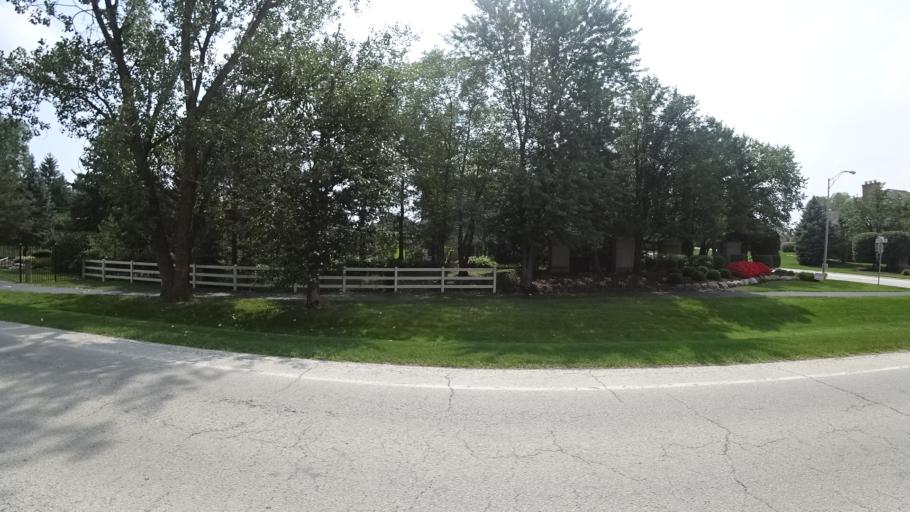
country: US
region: Illinois
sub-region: Will County
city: Goodings Grove
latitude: 41.6150
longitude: -87.9030
